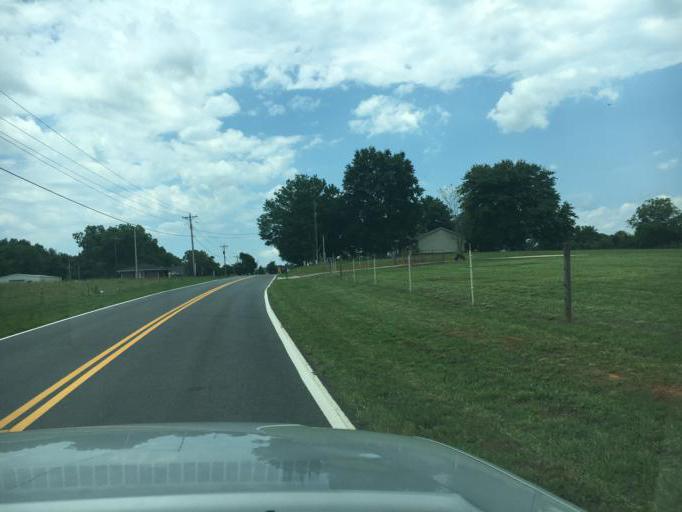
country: US
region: South Carolina
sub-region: Spartanburg County
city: Duncan
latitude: 34.8729
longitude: -82.1685
